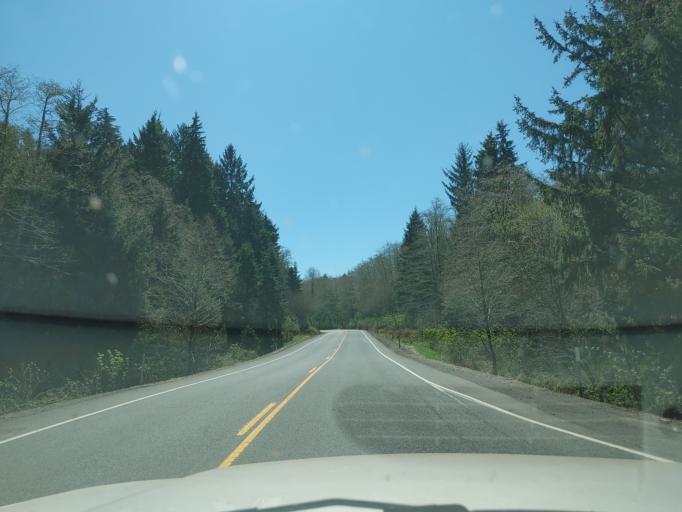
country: US
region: Oregon
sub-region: Clatsop County
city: Warrenton
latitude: 46.1487
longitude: -123.9019
